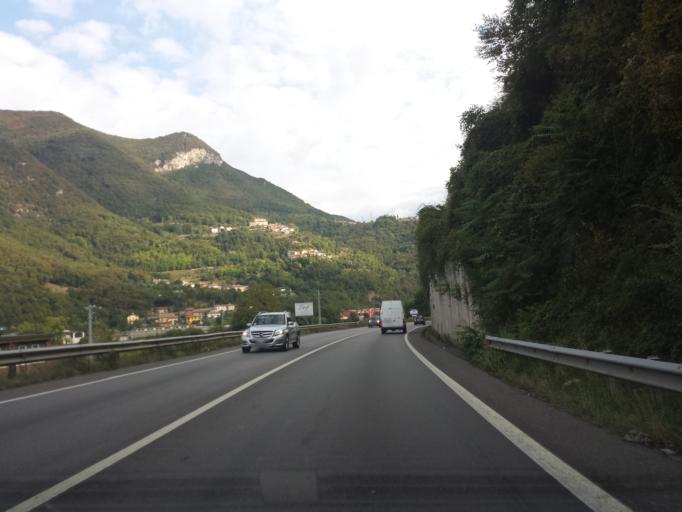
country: IT
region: Lombardy
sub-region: Provincia di Brescia
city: Villanuova sul Clisi
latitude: 45.6005
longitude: 10.4612
